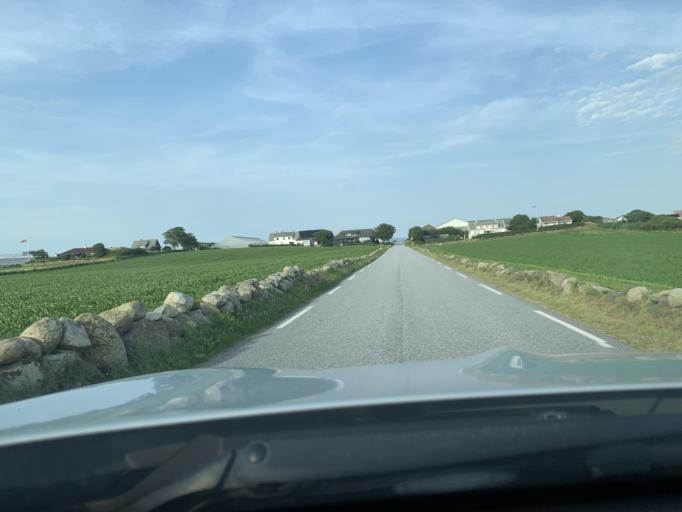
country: NO
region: Rogaland
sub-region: Klepp
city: Kleppe
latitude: 58.7161
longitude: 5.5363
